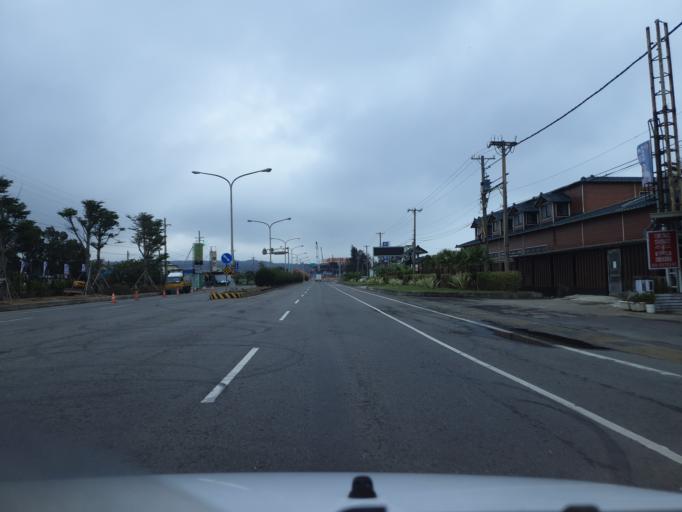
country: TW
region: Taiwan
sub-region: Hsinchu
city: Zhubei
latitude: 24.9051
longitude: 120.9746
